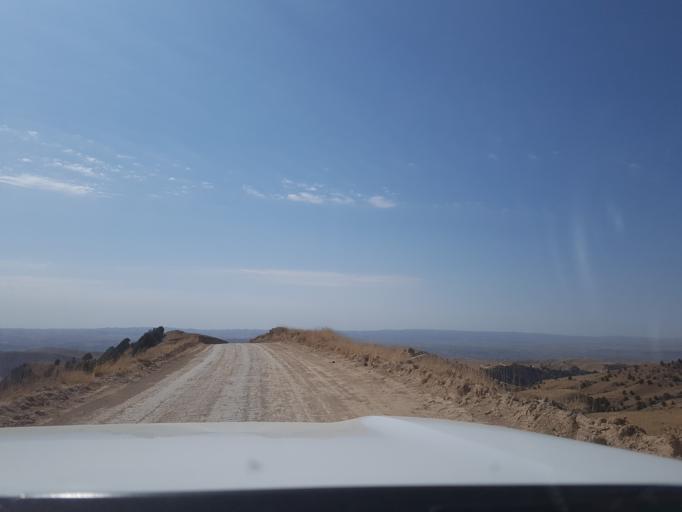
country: TM
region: Ahal
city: Baharly
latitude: 38.2907
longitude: 56.9334
